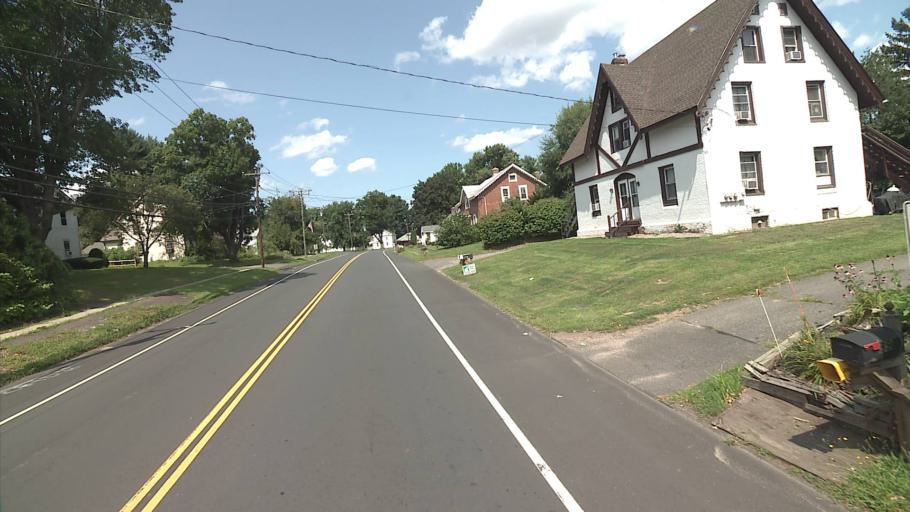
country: US
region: Connecticut
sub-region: Hartford County
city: Broad Brook
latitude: 41.9185
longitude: -72.5460
